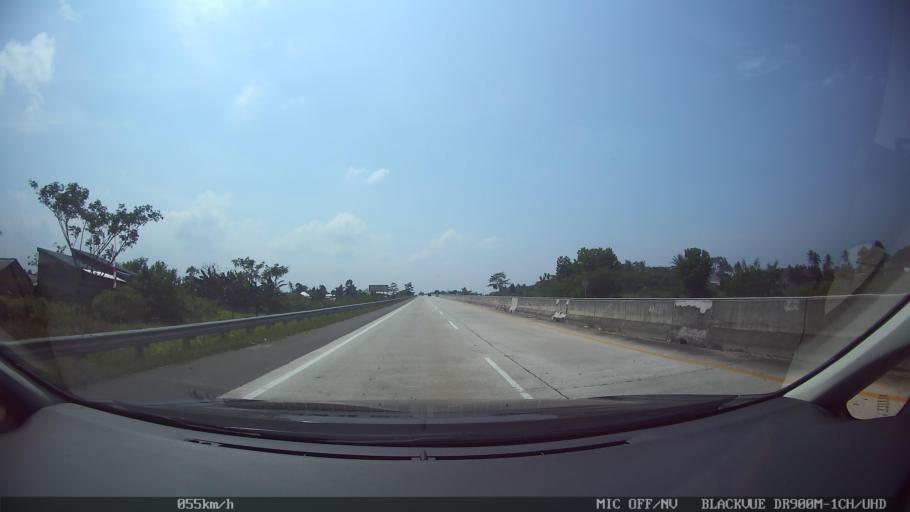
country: ID
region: Lampung
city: Kedaton
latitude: -5.3241
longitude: 105.2775
